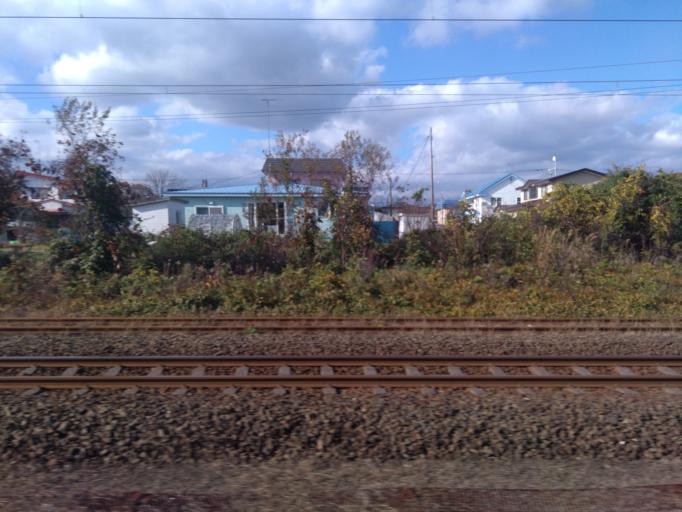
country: JP
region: Hokkaido
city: Shiraoi
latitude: 42.5206
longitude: 141.3046
